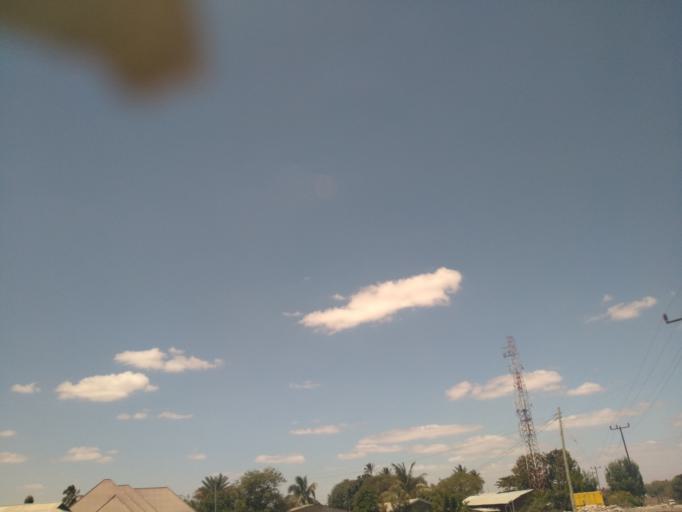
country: TZ
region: Dodoma
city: Dodoma
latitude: -6.1874
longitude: 35.7334
